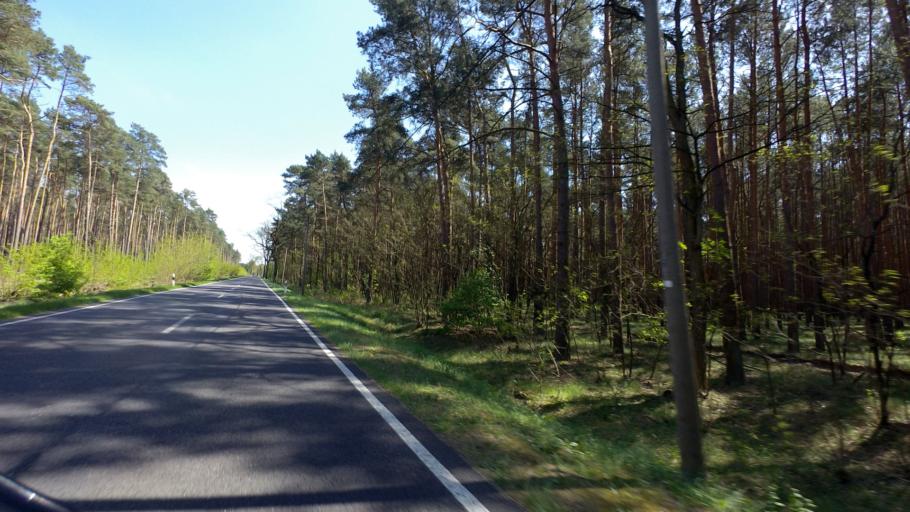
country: DE
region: Brandenburg
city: Neu Zauche
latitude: 51.9970
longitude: 14.0803
